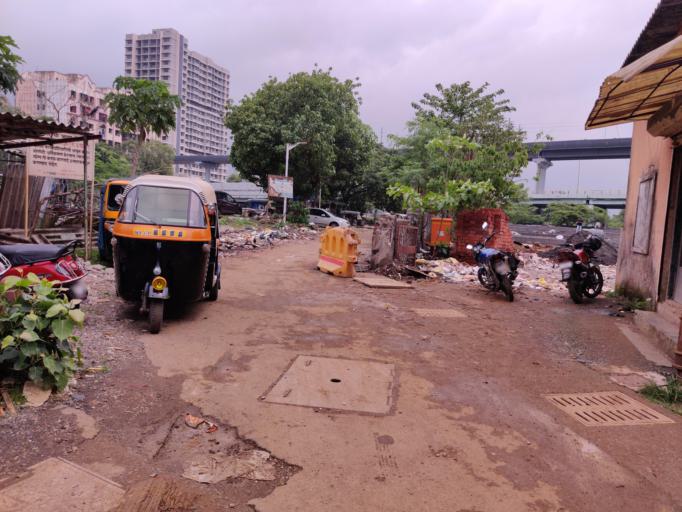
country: IN
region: Maharashtra
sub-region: Mumbai Suburban
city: Borivli
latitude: 19.2575
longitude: 72.8565
